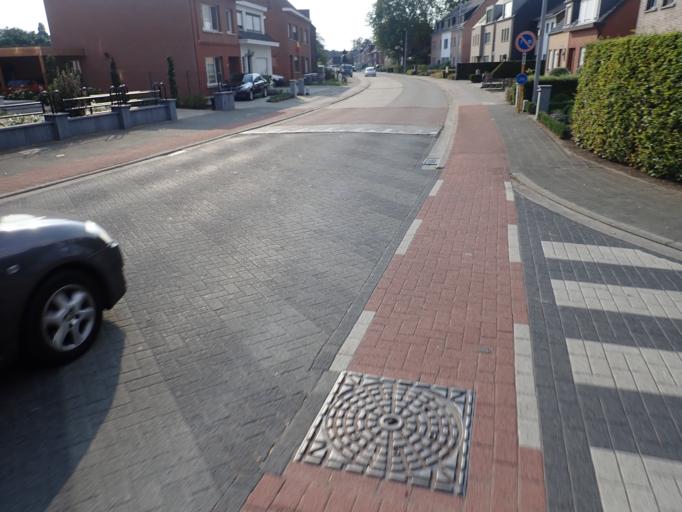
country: BE
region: Flanders
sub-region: Provincie Antwerpen
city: Herenthout
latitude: 51.1407
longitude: 4.7516
